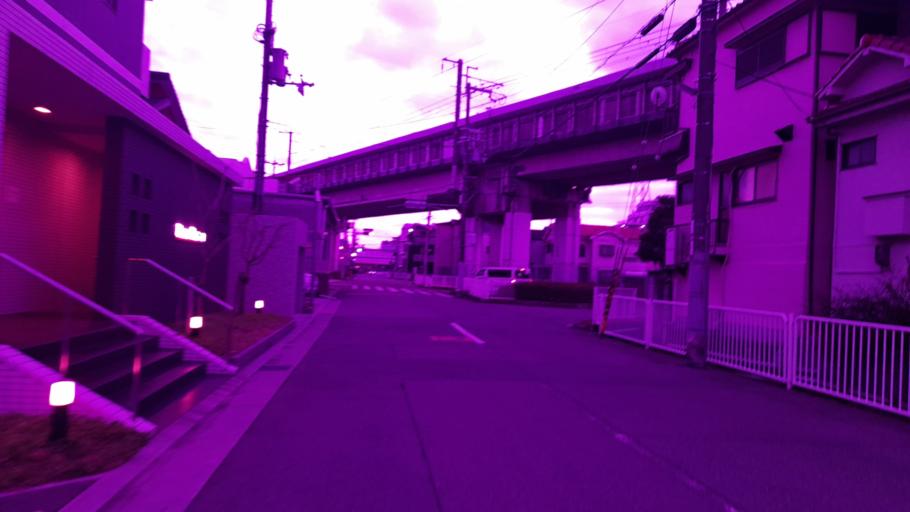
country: JP
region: Hyogo
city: Amagasaki
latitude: 34.7472
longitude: 135.4452
